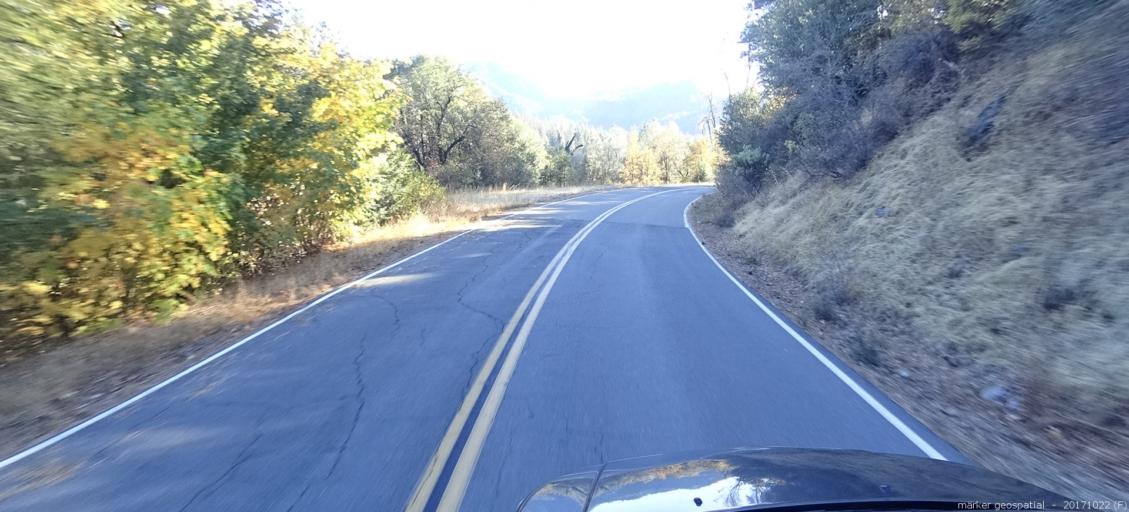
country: US
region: California
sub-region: Shasta County
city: Bella Vista
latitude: 40.8766
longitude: -122.2342
